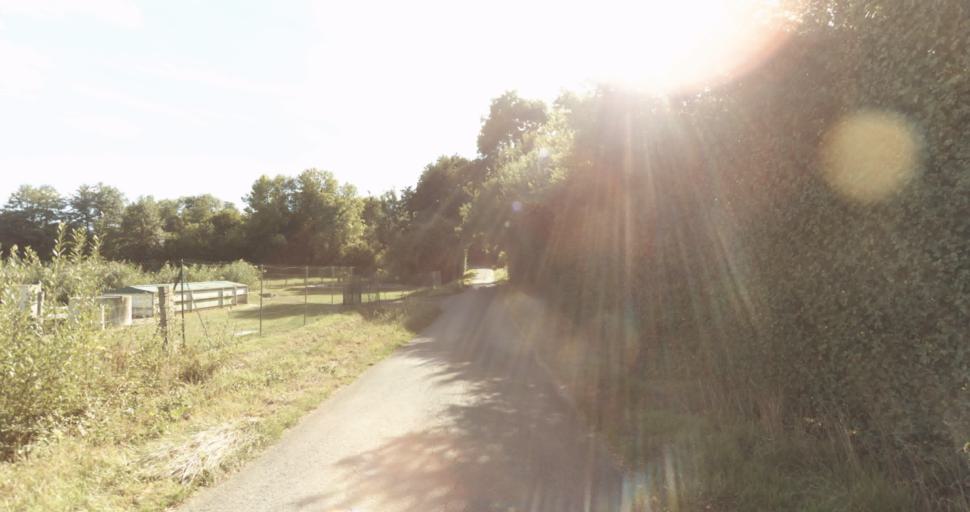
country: FR
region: Lower Normandy
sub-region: Departement de l'Orne
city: Vimoutiers
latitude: 48.9213
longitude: 0.1322
